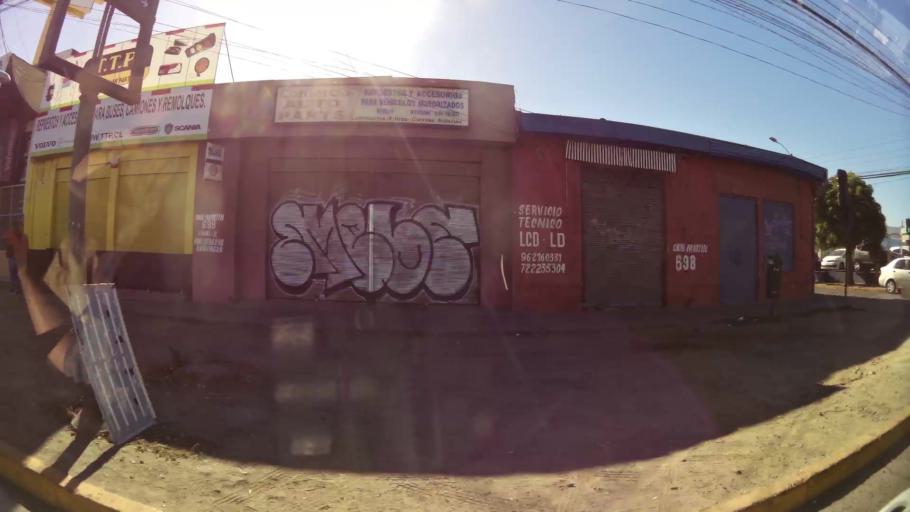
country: CL
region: O'Higgins
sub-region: Provincia de Cachapoal
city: Rancagua
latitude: -34.1726
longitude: -70.7469
